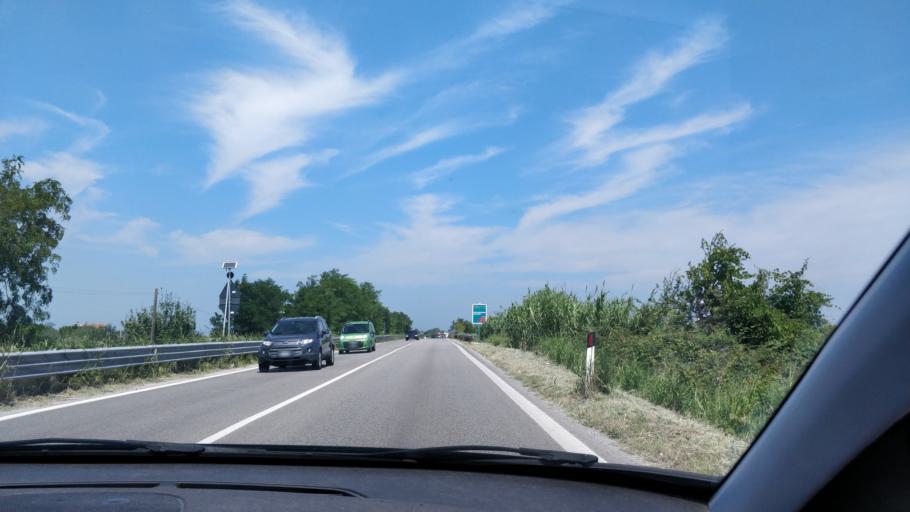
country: IT
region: Abruzzo
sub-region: Provincia di Chieti
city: Ortona
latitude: 42.3627
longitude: 14.3829
